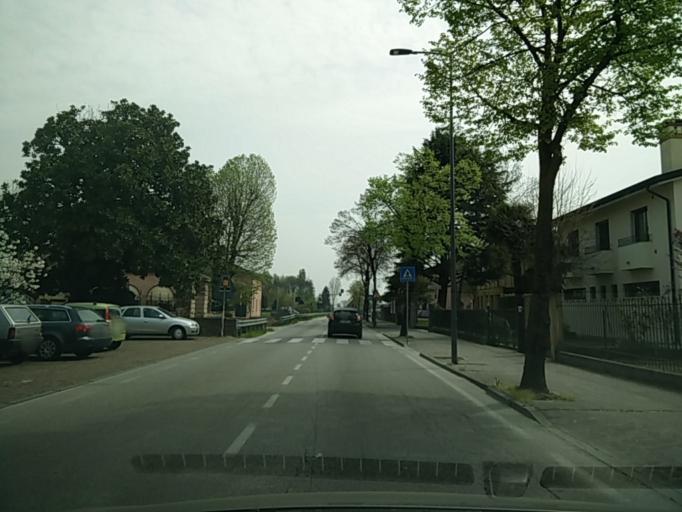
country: IT
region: Veneto
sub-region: Provincia di Venezia
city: Caltana
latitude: 45.4790
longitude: 12.0308
